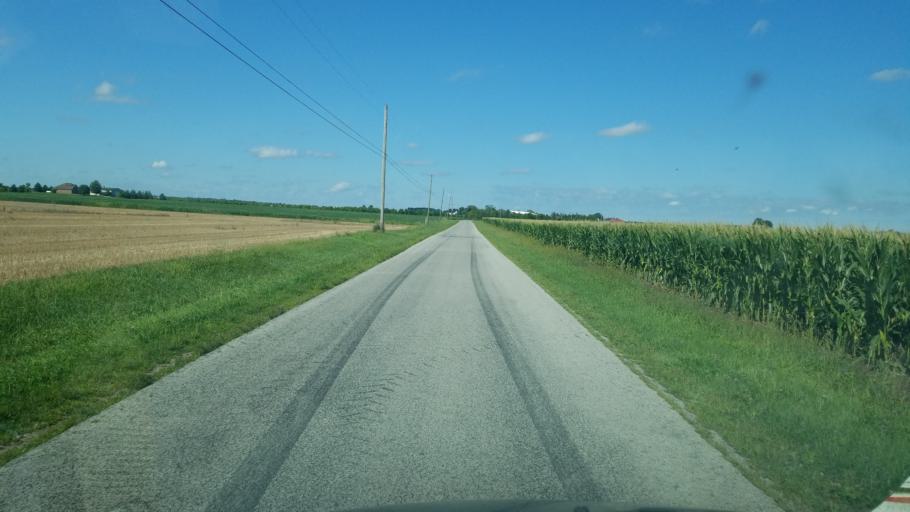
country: US
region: Ohio
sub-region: Hancock County
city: McComb
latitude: 41.1243
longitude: -83.7328
